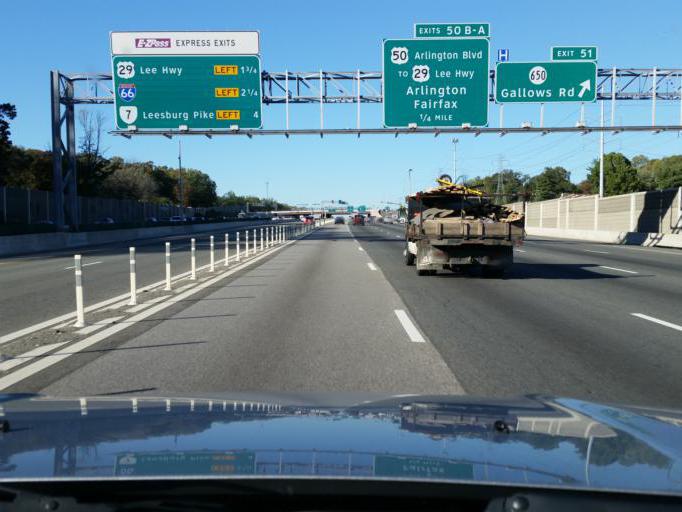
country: US
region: Virginia
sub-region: Fairfax County
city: Merrifield
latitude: 38.8482
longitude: -77.2198
